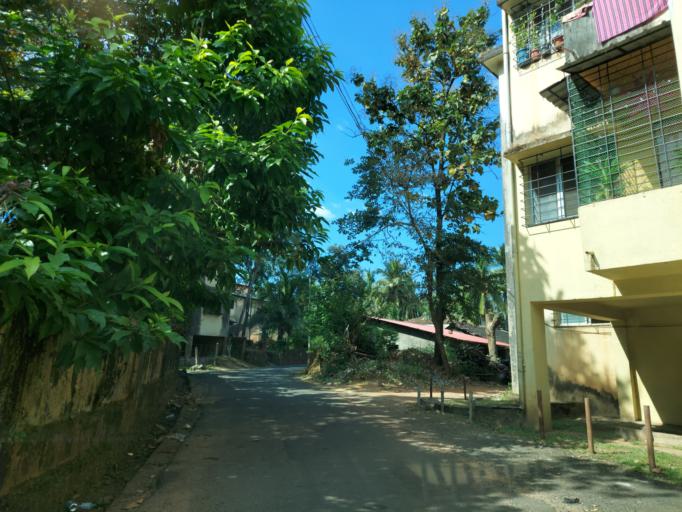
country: IN
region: Maharashtra
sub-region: Sindhudurg
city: Savantvadi
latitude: 15.9042
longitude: 73.8168
